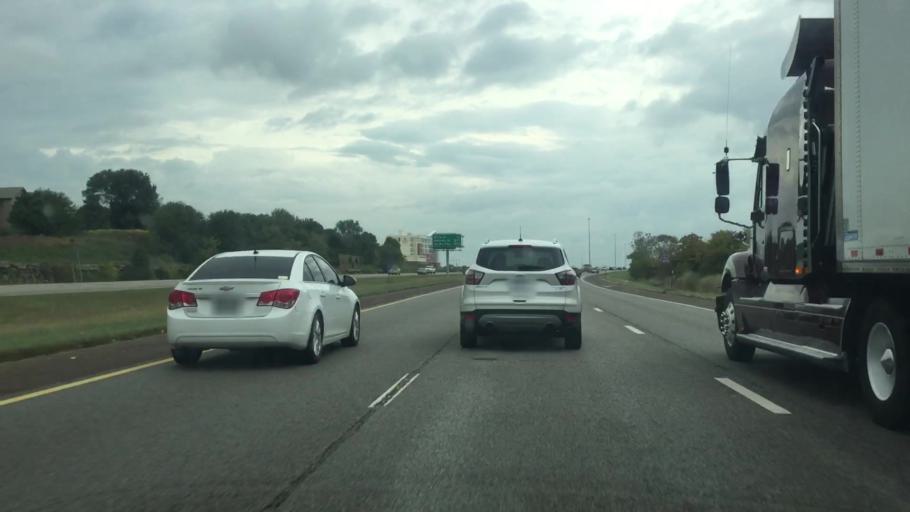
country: US
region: Kansas
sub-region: Johnson County
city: Lenexa
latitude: 38.9640
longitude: -94.7760
